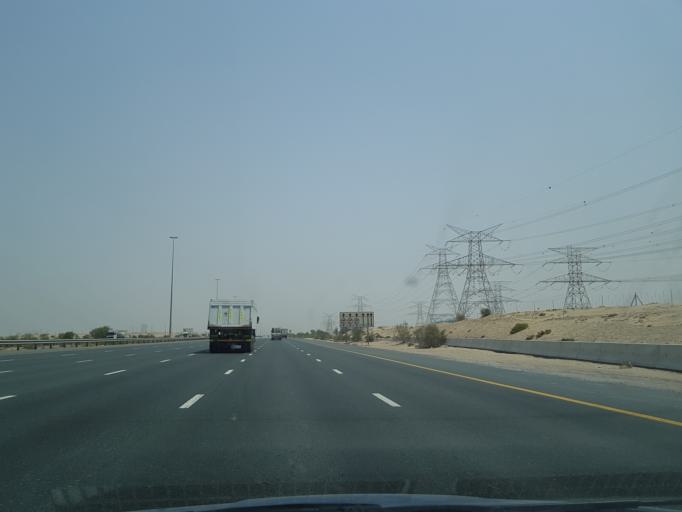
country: AE
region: Dubai
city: Dubai
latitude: 25.0448
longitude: 55.3047
